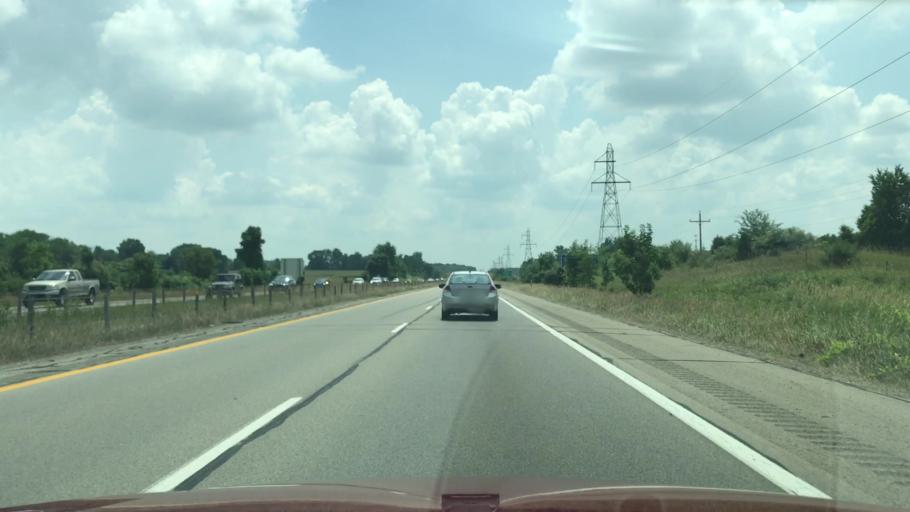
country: US
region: Michigan
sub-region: Kent County
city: Cutlerville
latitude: 42.7944
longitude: -85.6687
